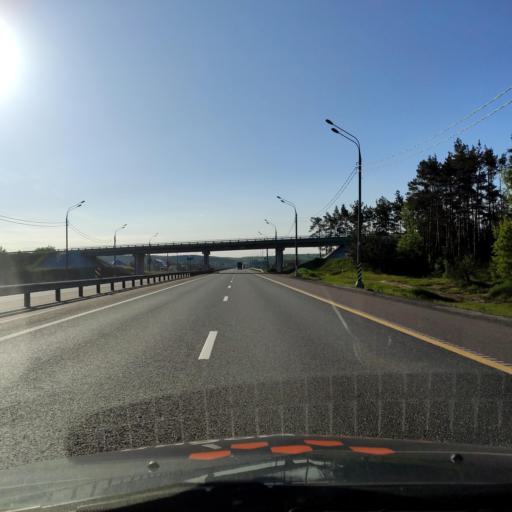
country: RU
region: Lipetsk
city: Zadonsk
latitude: 52.3771
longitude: 38.8883
